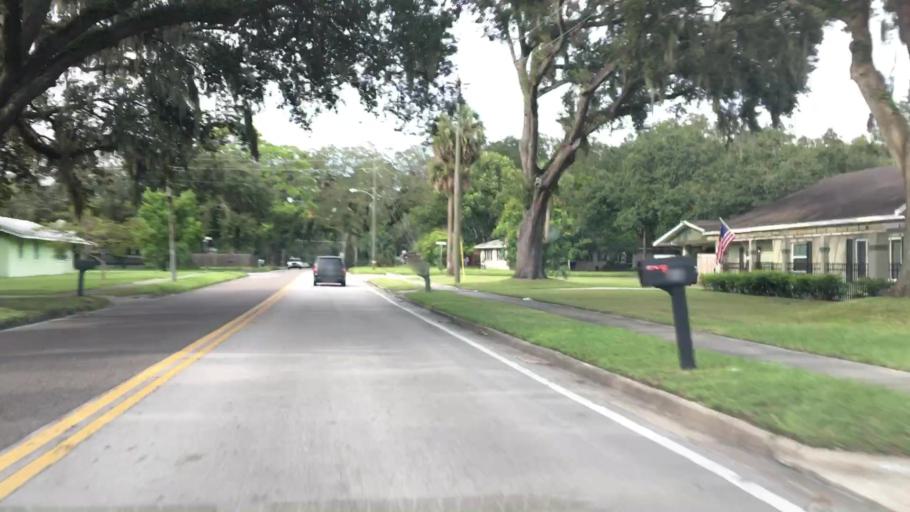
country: US
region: Florida
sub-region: Seminole County
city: Sanford
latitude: 28.7896
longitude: -81.2648
